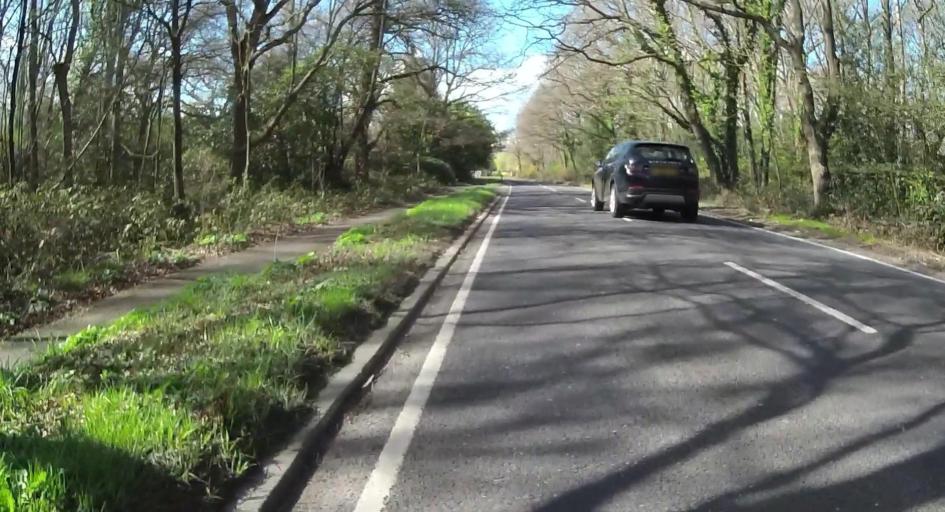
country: GB
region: England
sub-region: Surrey
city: Chobham
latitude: 51.3423
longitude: -0.5925
